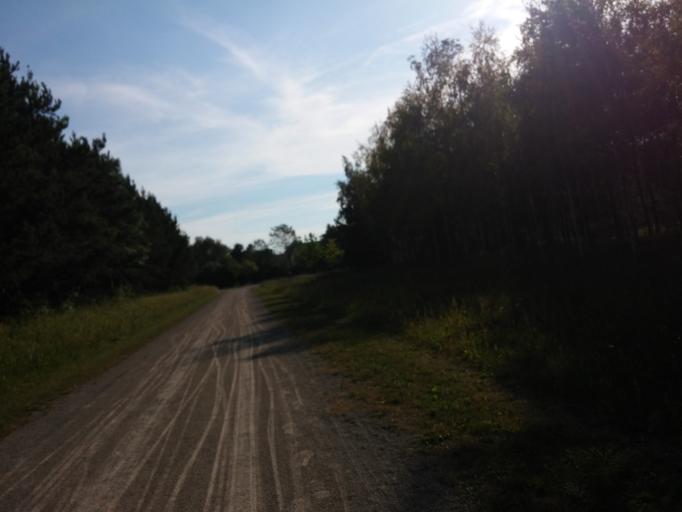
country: DE
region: Bavaria
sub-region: Upper Bavaria
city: Haar
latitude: 48.1239
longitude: 11.7028
